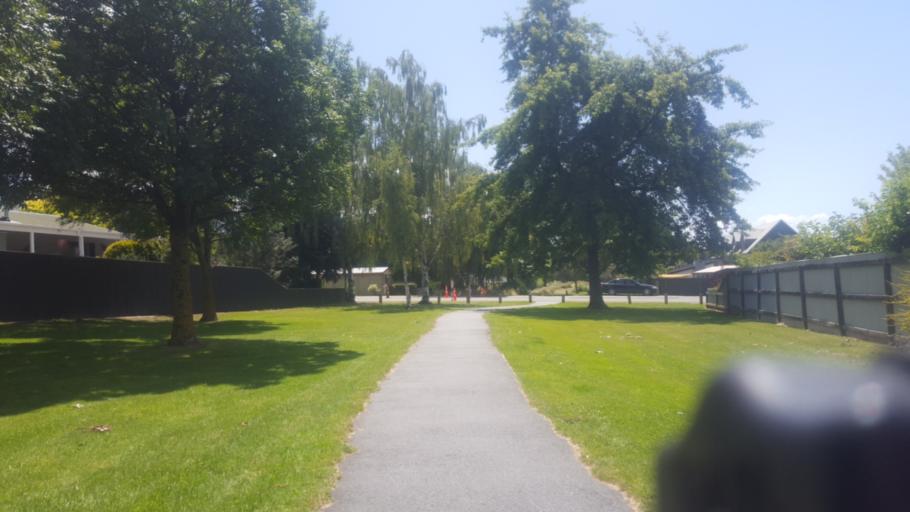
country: NZ
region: Otago
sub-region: Queenstown-Lakes District
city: Wanaka
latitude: -45.0448
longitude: 169.1984
